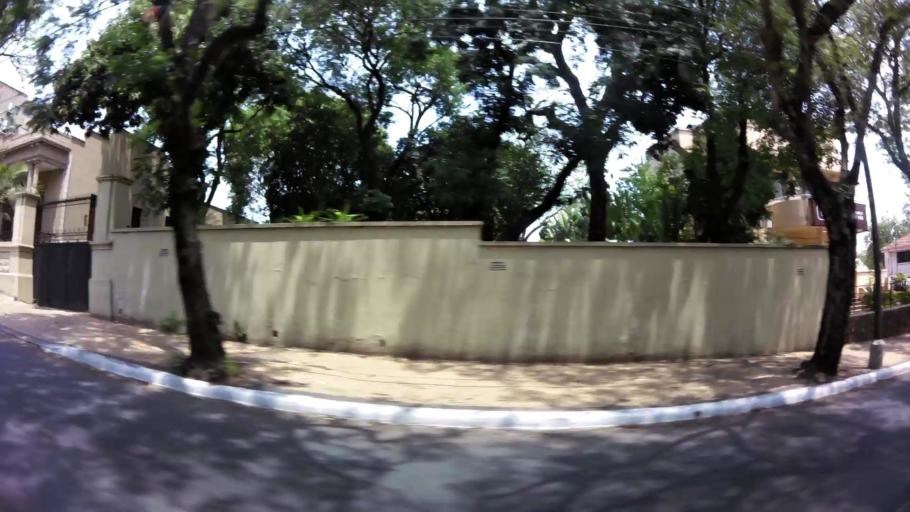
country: PY
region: Asuncion
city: Asuncion
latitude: -25.2927
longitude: -57.6137
